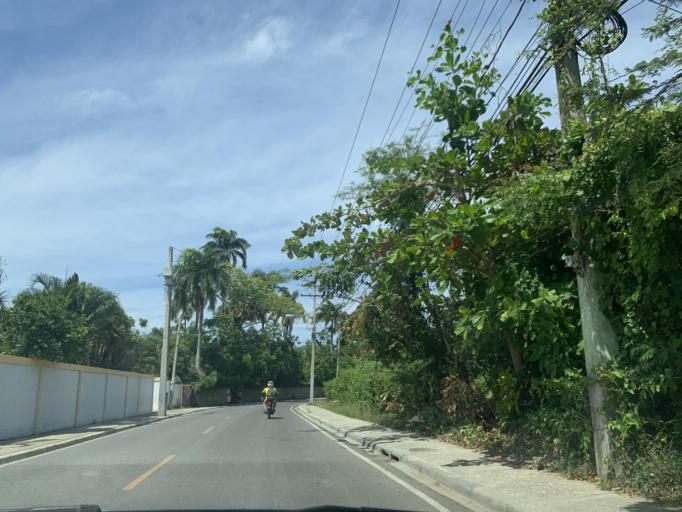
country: DO
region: Puerto Plata
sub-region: Puerto Plata
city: Puerto Plata
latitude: 19.8035
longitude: -70.7184
